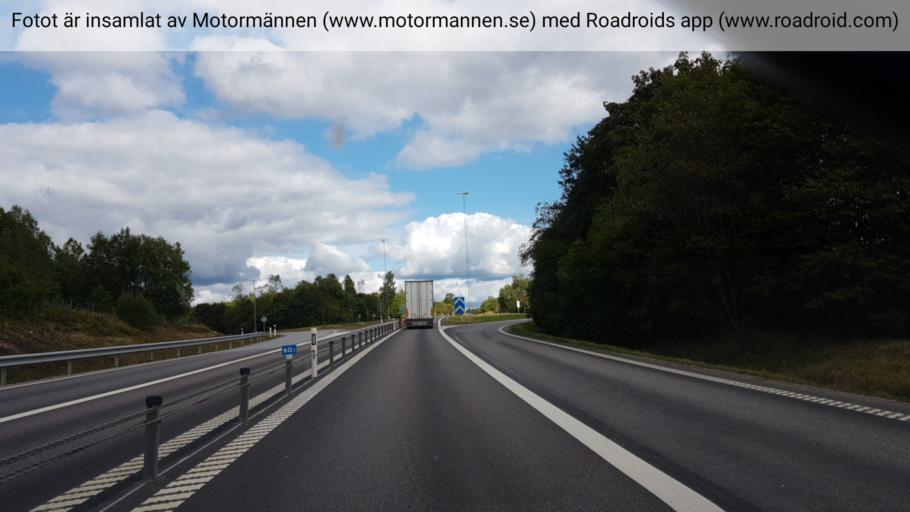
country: SE
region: Joenkoeping
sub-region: Tranas Kommun
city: Tranas
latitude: 58.0204
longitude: 14.9416
